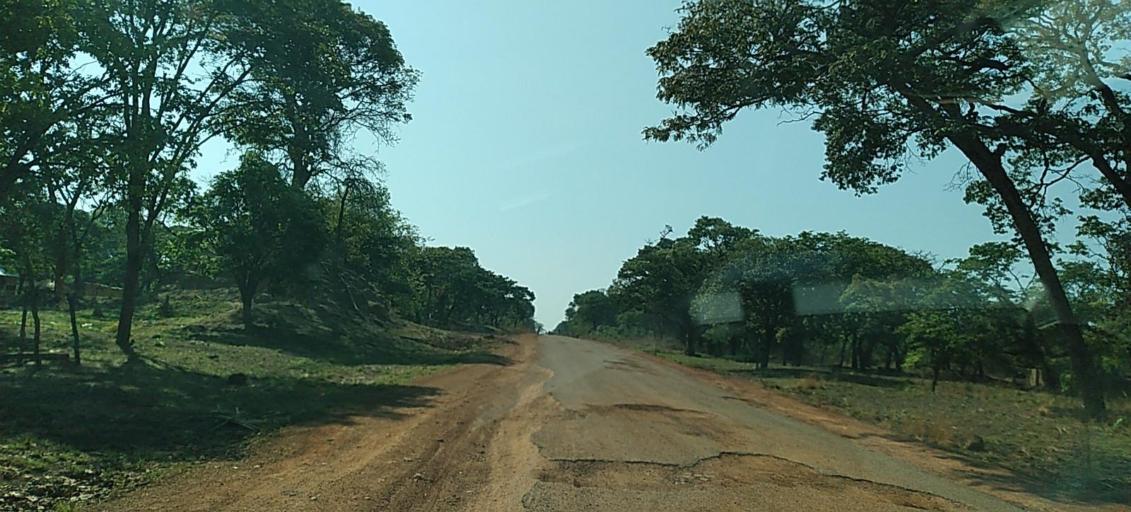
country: ZM
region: North-Western
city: Mwinilunga
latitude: -11.9046
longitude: 25.2860
